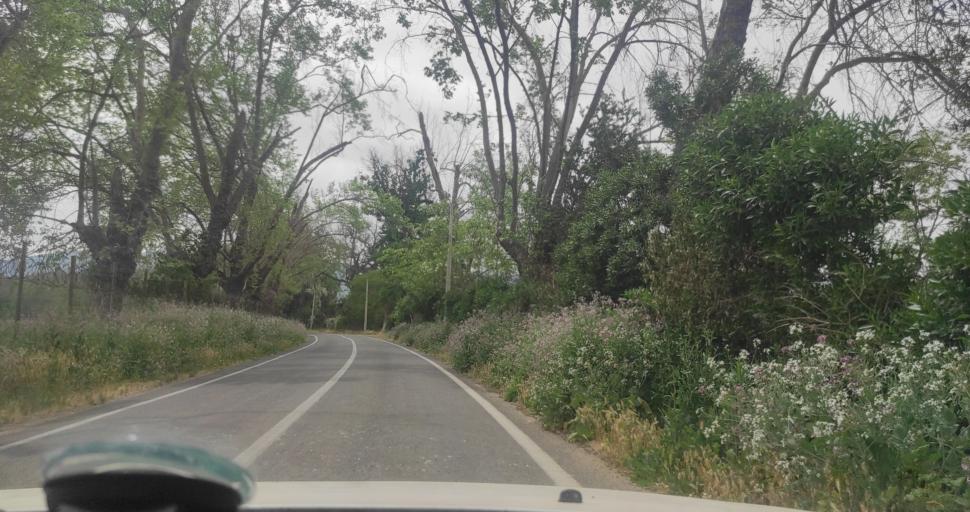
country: CL
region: Valparaiso
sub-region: Provincia de Marga Marga
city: Limache
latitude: -33.0284
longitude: -71.2394
